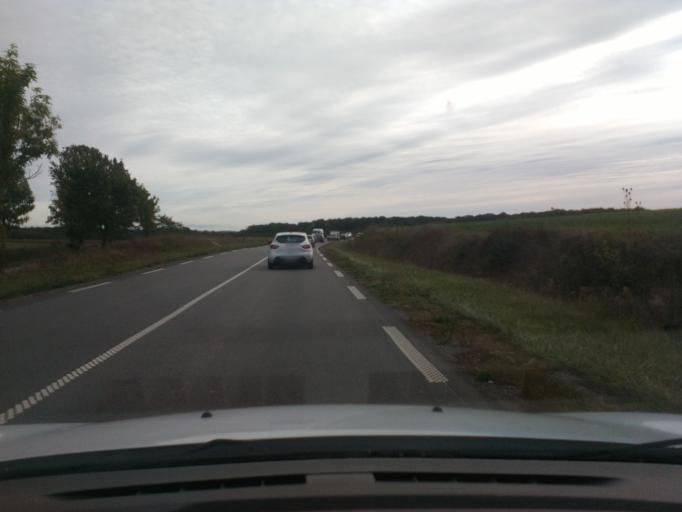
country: FR
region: Lorraine
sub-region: Departement des Vosges
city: Aydoilles
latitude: 48.2749
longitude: 6.5630
